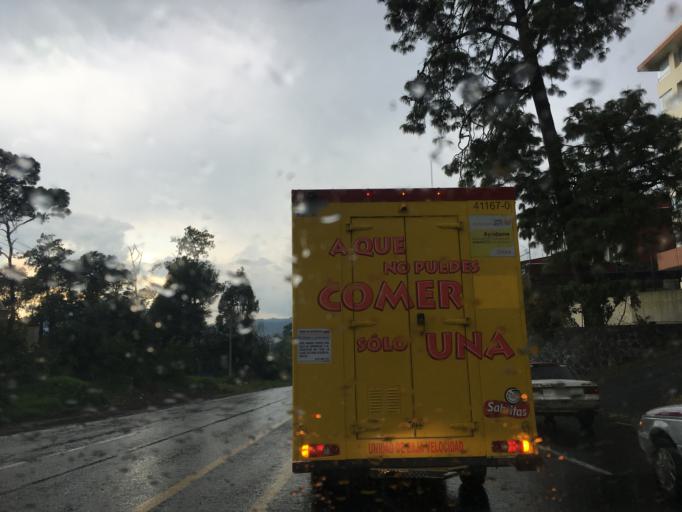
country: MX
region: Michoacan
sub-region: Uruapan
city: Uruapan
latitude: 19.4359
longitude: -102.0728
